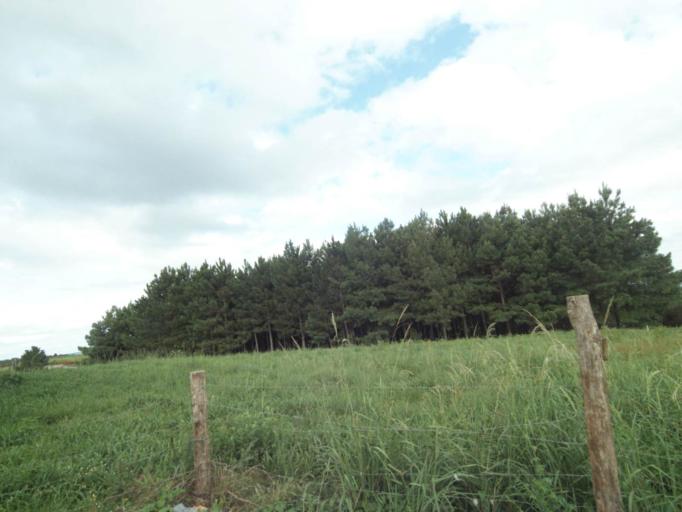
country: BR
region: Rio Grande do Sul
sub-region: Lagoa Vermelha
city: Lagoa Vermelha
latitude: -28.2061
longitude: -51.5141
